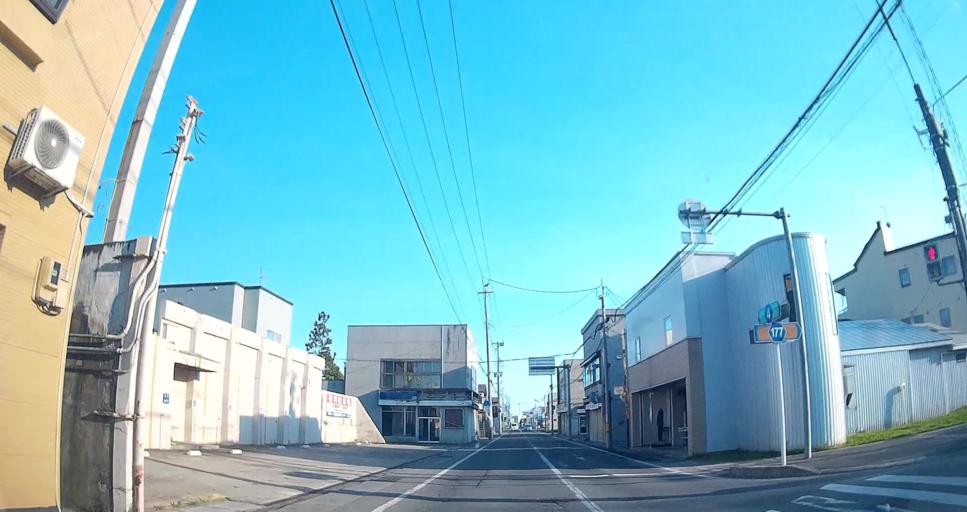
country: JP
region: Aomori
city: Mutsu
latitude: 41.2925
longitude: 141.2106
